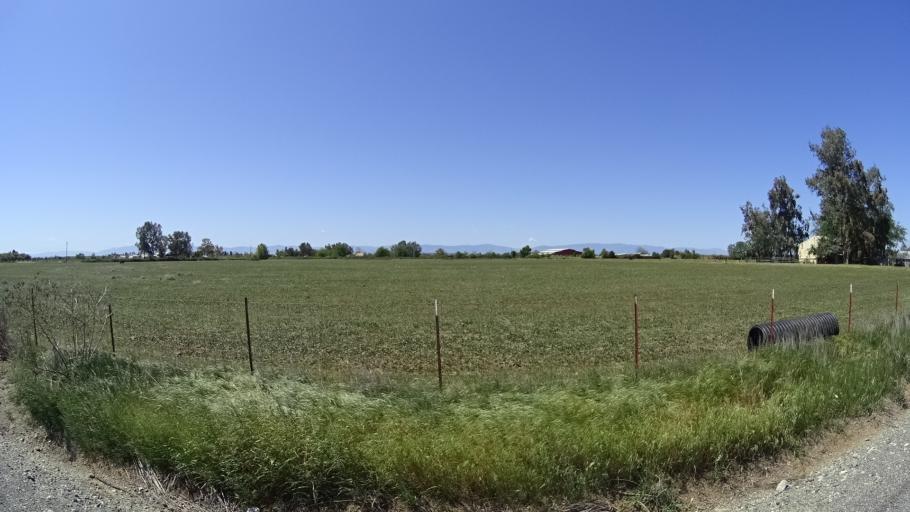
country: US
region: California
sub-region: Glenn County
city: Orland
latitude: 39.7890
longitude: -122.1785
